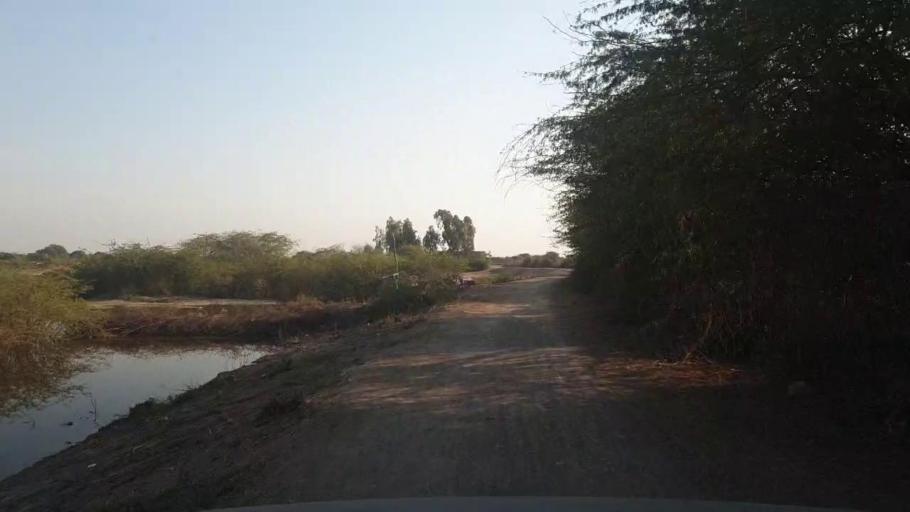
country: PK
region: Sindh
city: Chambar
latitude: 25.2564
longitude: 68.8985
